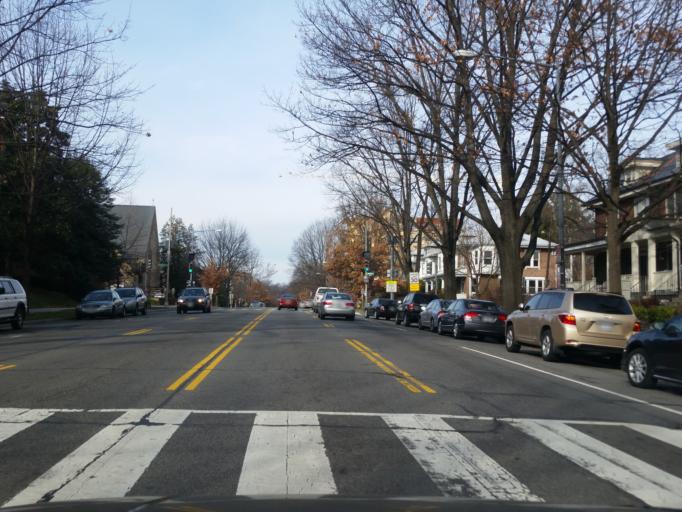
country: US
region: Maryland
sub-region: Montgomery County
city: Chevy Chase Village
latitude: 38.9583
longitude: -77.0717
